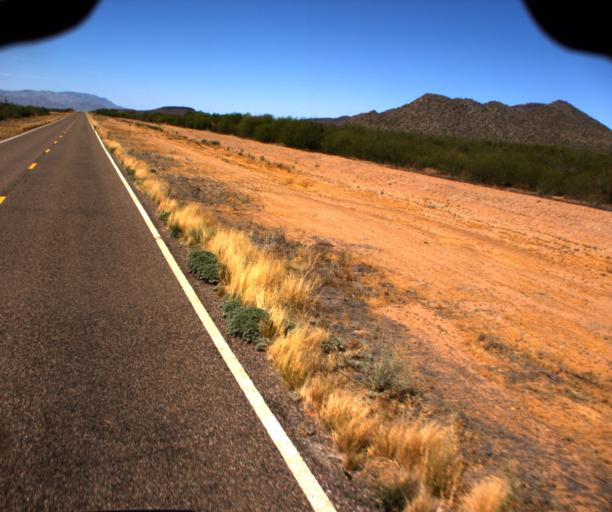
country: US
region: Arizona
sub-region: Yavapai County
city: Congress
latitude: 34.0376
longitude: -113.0746
